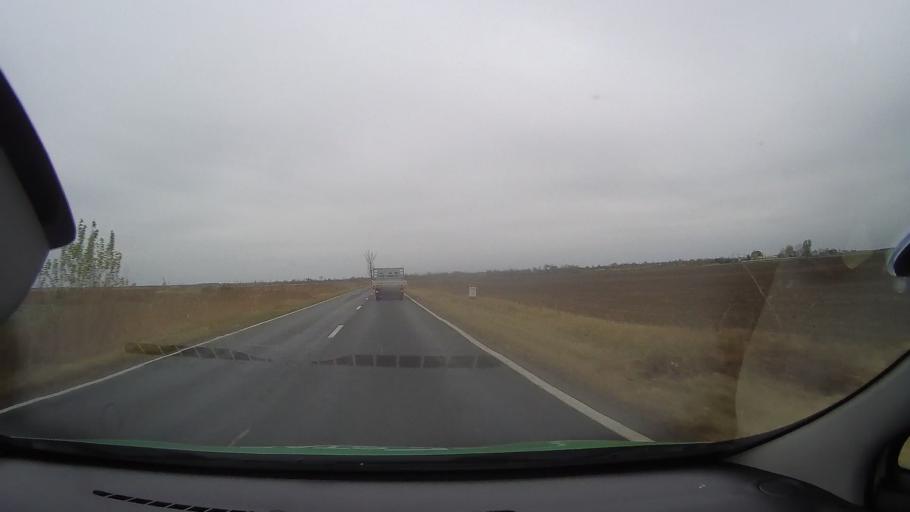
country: RO
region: Ialomita
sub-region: Comuna Scanteia
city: Iazu
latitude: 44.7357
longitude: 27.4335
